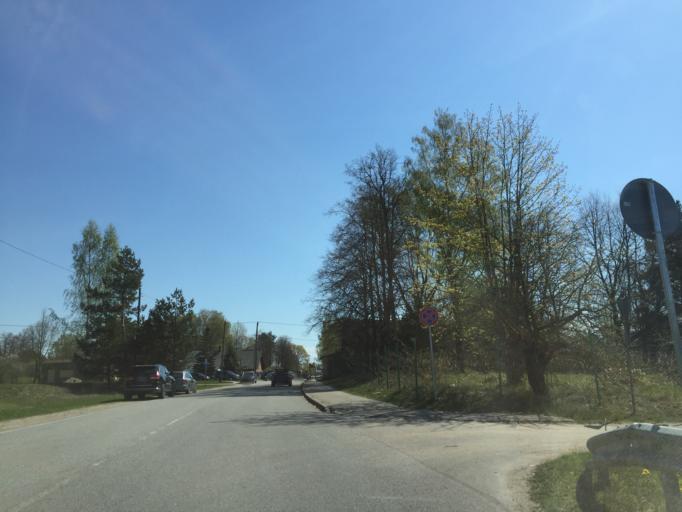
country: LV
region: Saulkrastu
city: Saulkrasti
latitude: 57.3306
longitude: 24.4397
